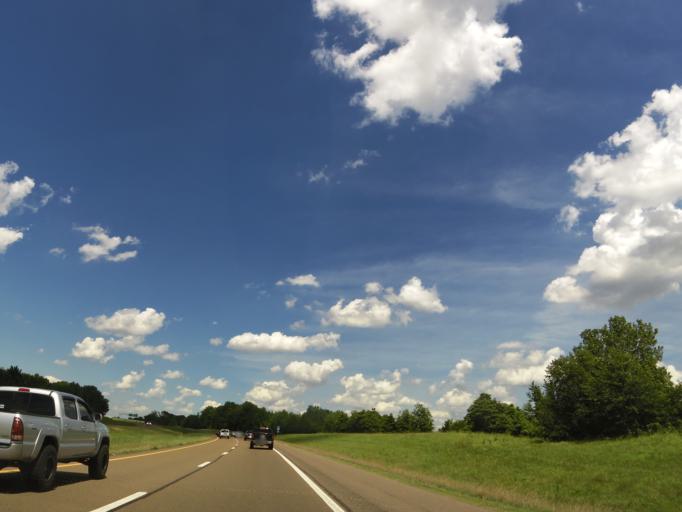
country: US
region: Tennessee
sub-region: Dyer County
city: Dyersburg
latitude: 36.0678
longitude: -89.3570
